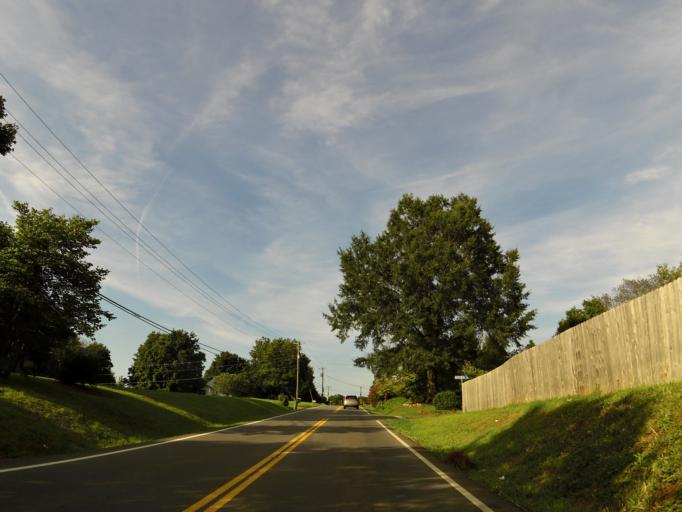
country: US
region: Tennessee
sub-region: Sevier County
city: Seymour
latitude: 35.8667
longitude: -83.7645
